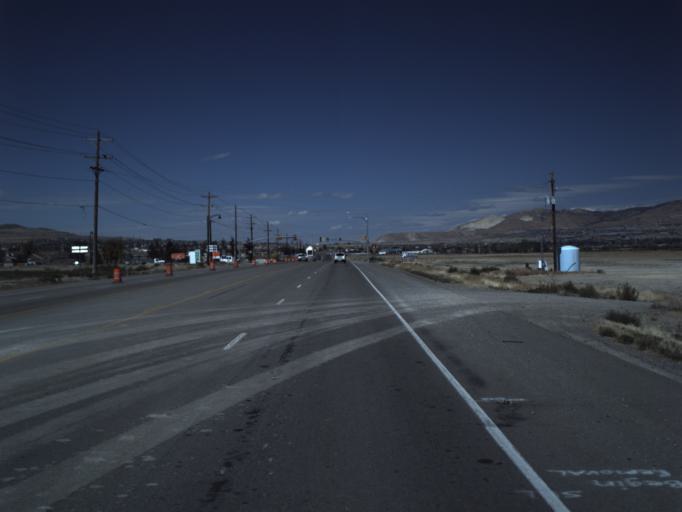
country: US
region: Utah
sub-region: Utah County
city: Saratoga Springs
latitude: 40.3592
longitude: -111.9162
